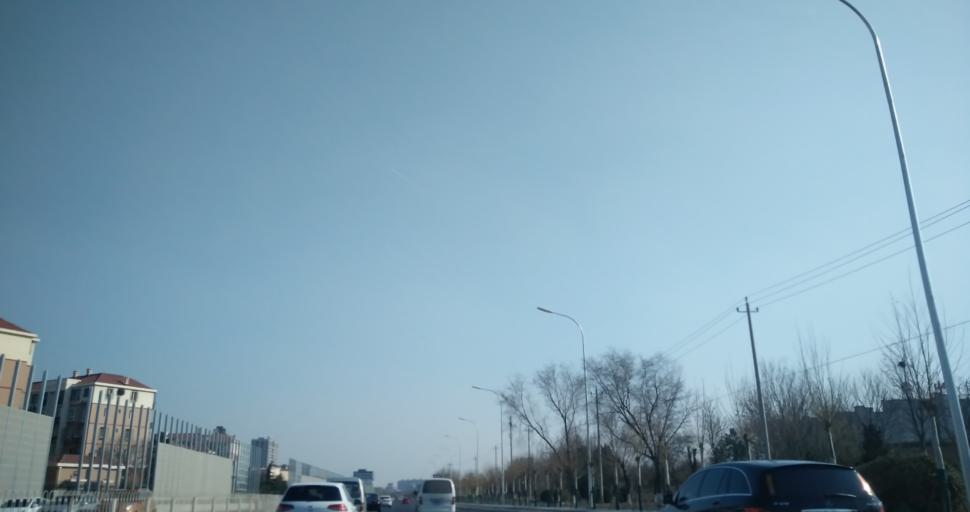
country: CN
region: Beijing
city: Jiugong
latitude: 39.7892
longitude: 116.4814
